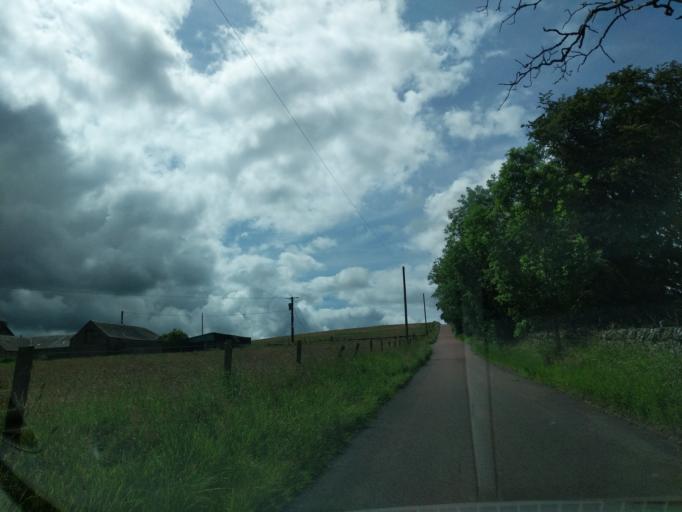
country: GB
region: Scotland
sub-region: South Lanarkshire
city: Carnwath
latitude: 55.6284
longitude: -3.6756
